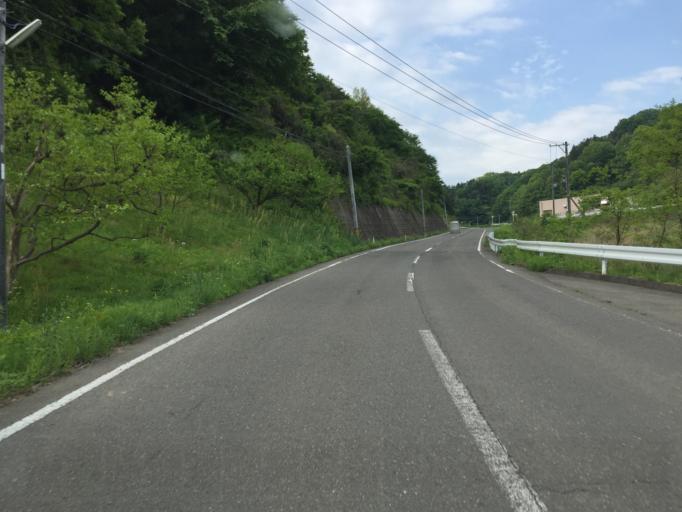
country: JP
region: Fukushima
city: Hobaramachi
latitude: 37.7090
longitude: 140.5849
